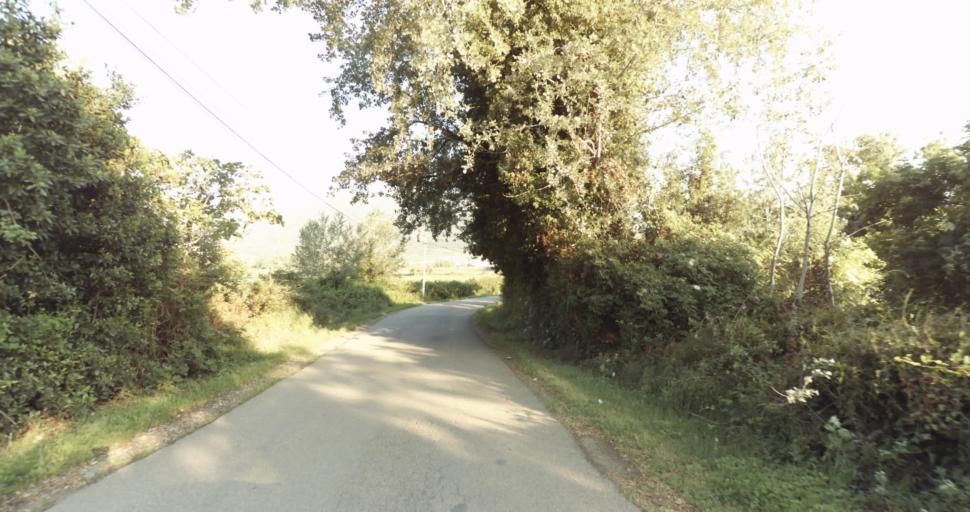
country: FR
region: Corsica
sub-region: Departement de la Haute-Corse
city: Biguglia
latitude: 42.6098
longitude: 9.4432
